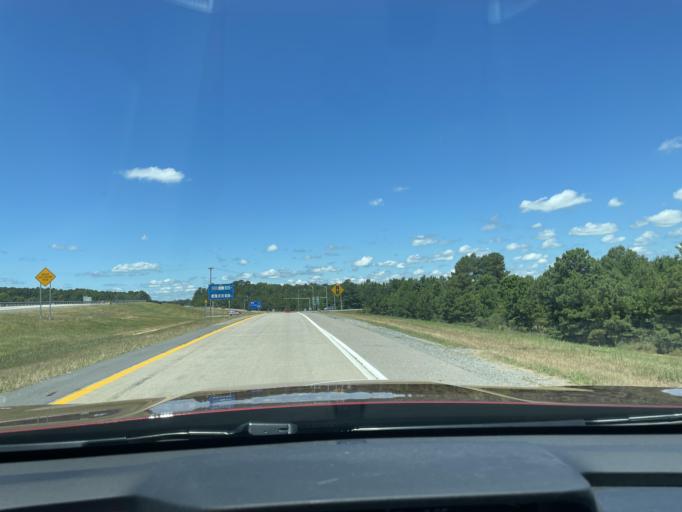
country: US
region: Arkansas
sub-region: Jefferson County
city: Pine Bluff
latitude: 34.1713
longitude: -92.0040
